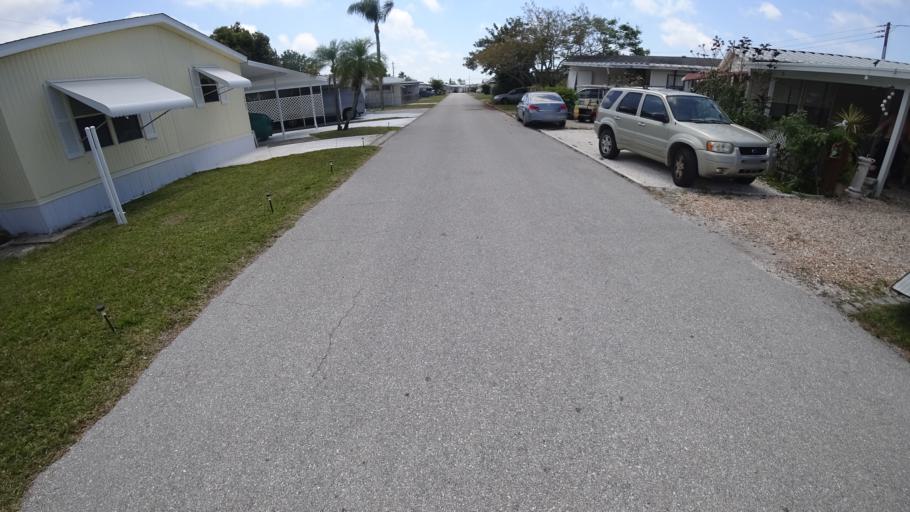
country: US
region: Florida
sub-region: Manatee County
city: Bayshore Gardens
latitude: 27.4241
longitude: -82.5790
